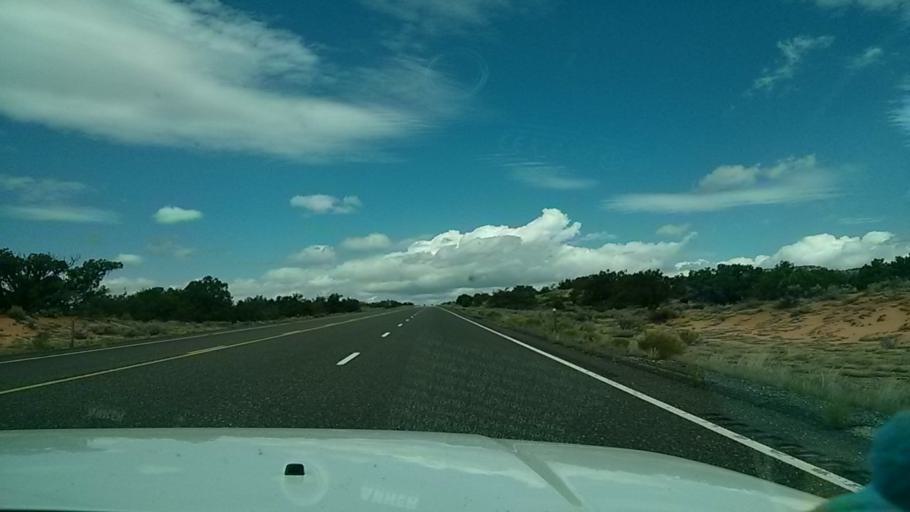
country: US
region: Utah
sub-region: Kane County
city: Kanab
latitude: 37.1627
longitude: -112.5929
